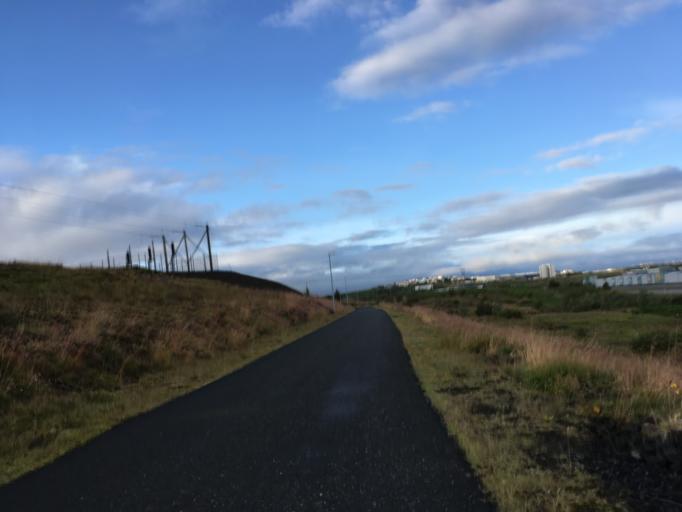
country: IS
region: Capital Region
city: Mosfellsbaer
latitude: 64.1469
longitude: -21.7453
